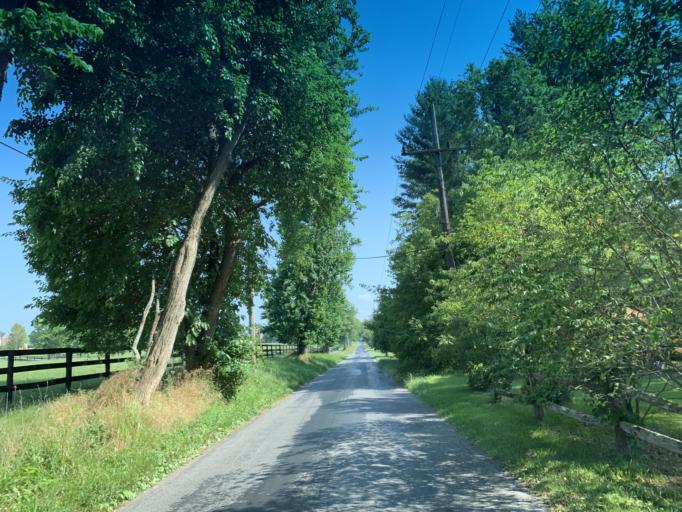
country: US
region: Maryland
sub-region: Montgomery County
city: Poolesville
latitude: 39.1474
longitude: -77.4539
